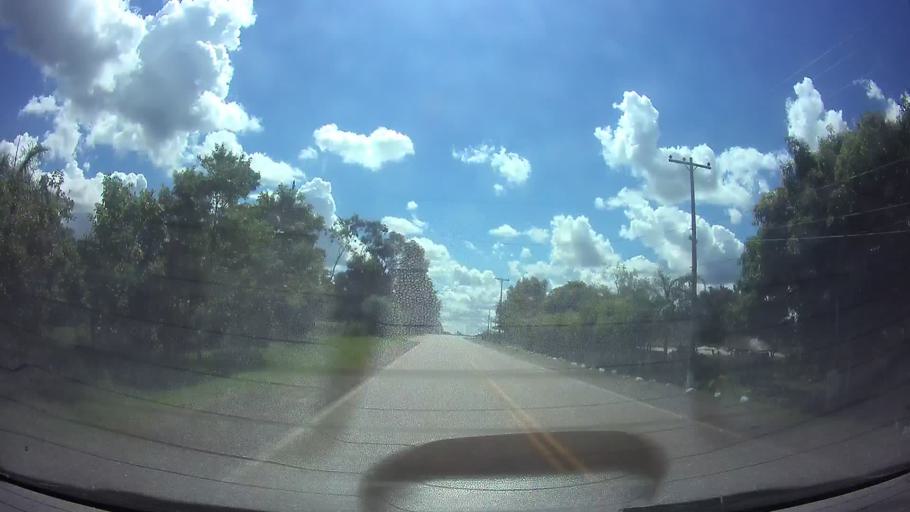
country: PY
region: Paraguari
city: La Colmena
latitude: -25.9114
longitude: -56.7555
